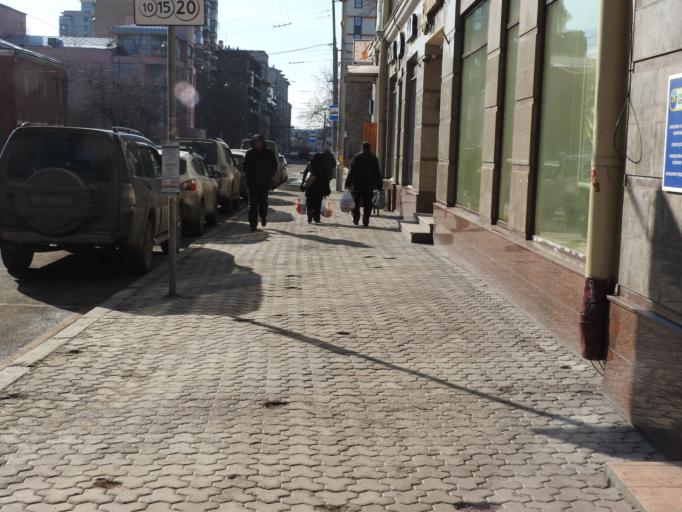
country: RU
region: Moscow
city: Mar'ina Roshcha
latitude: 55.7805
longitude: 37.5915
